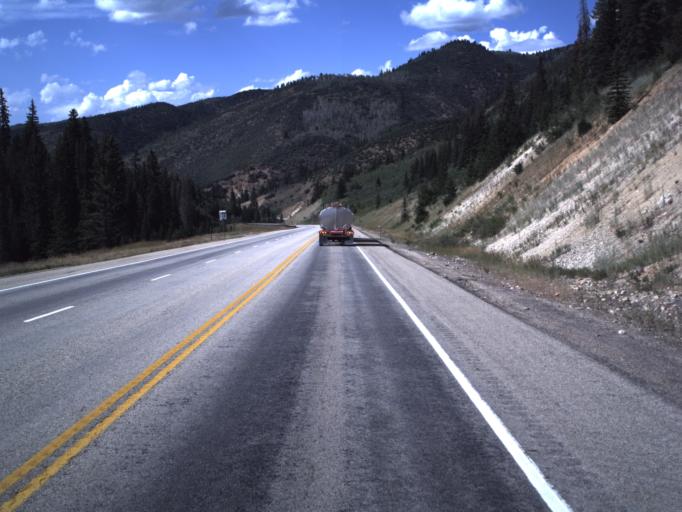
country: US
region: Utah
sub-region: Wasatch County
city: Heber
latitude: 40.3290
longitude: -111.2608
